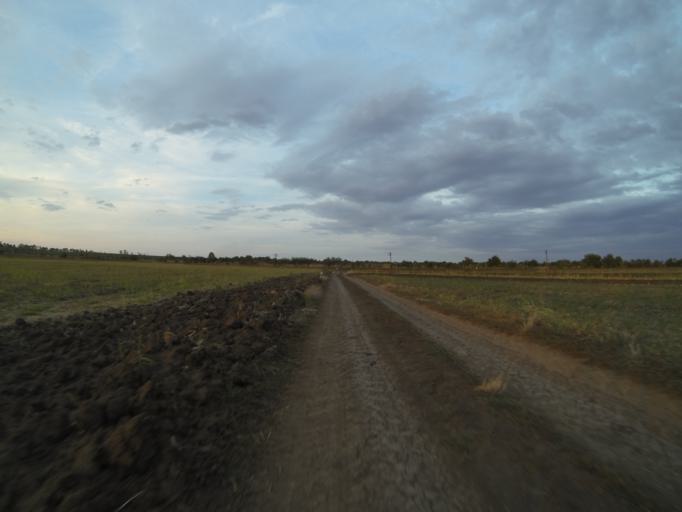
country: RO
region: Dolj
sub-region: Comuna Segarcea
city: Segarcea
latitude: 44.0969
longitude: 23.7241
